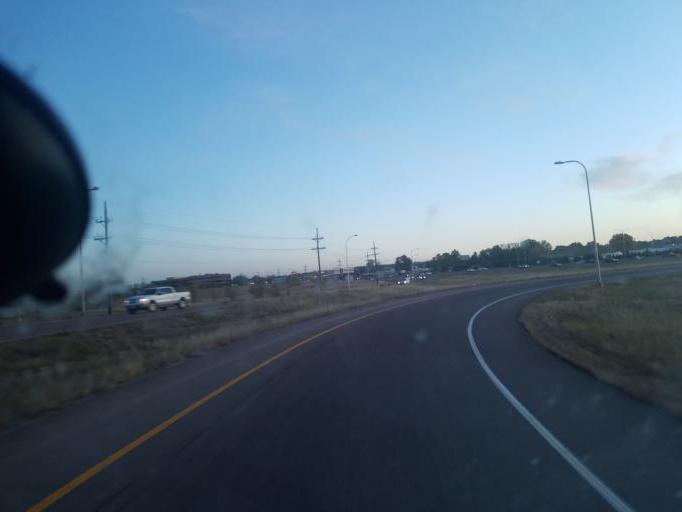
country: US
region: Colorado
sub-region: El Paso County
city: Cimarron Hills
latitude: 38.8402
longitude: -104.7227
